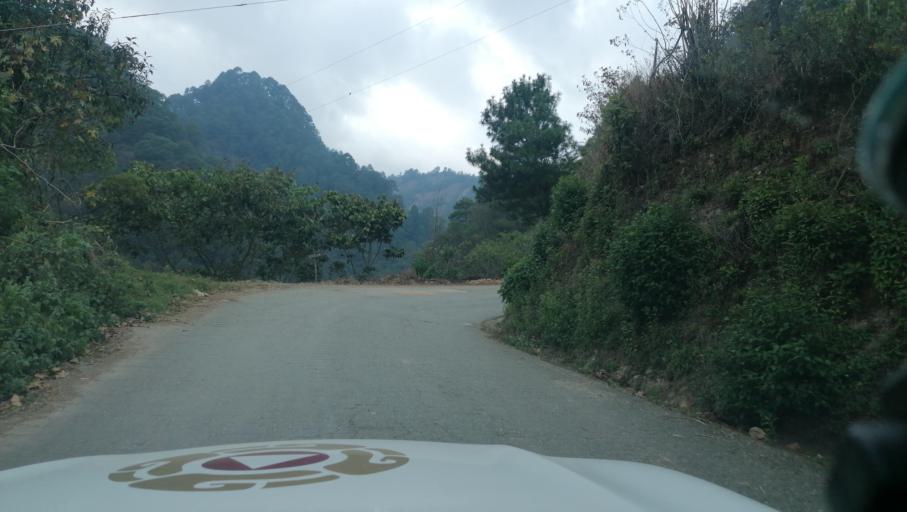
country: GT
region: San Marcos
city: Tacana
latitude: 15.2127
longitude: -92.1991
